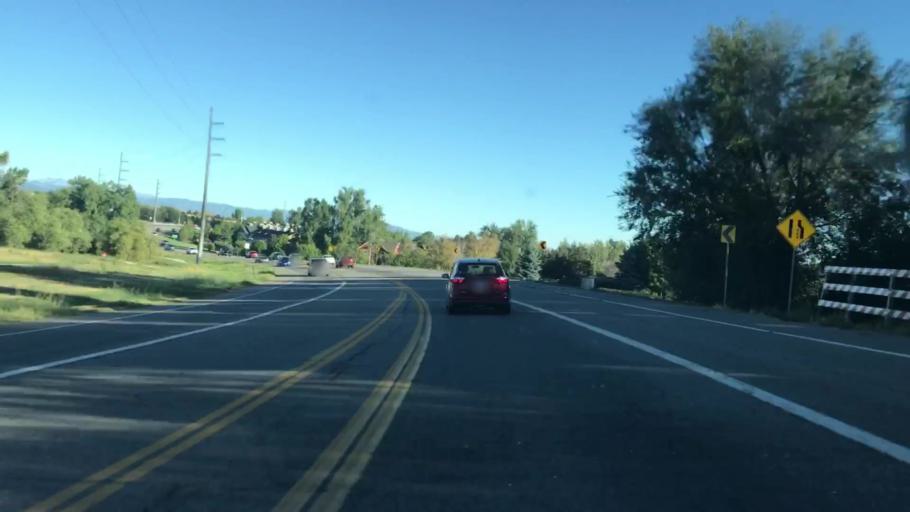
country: US
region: Colorado
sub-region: Boulder County
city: Louisville
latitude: 39.9961
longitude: -105.1277
